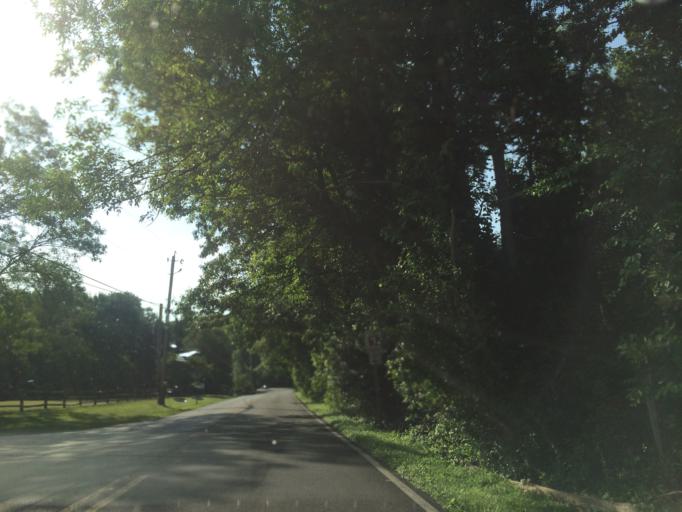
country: US
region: Maryland
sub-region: Howard County
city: Highland
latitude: 39.1978
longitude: -76.9967
